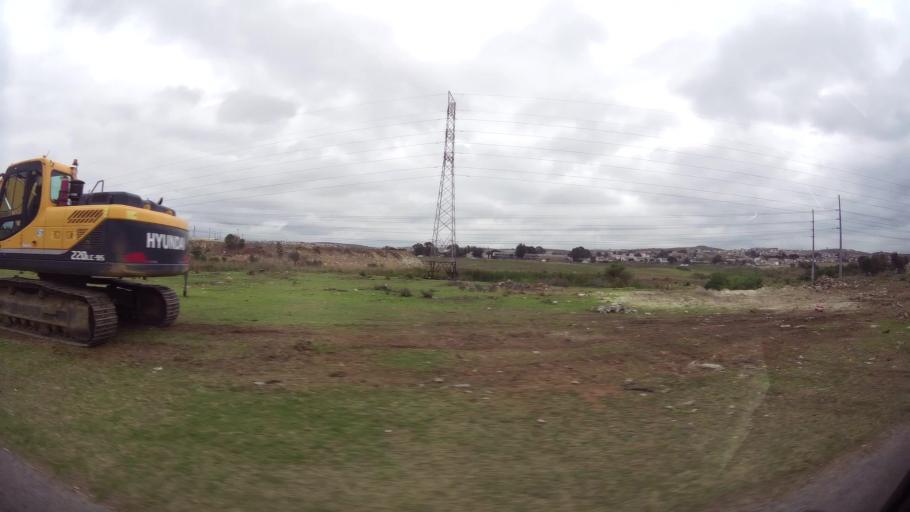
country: ZA
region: Eastern Cape
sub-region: Nelson Mandela Bay Metropolitan Municipality
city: Port Elizabeth
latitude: -33.9065
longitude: 25.5597
